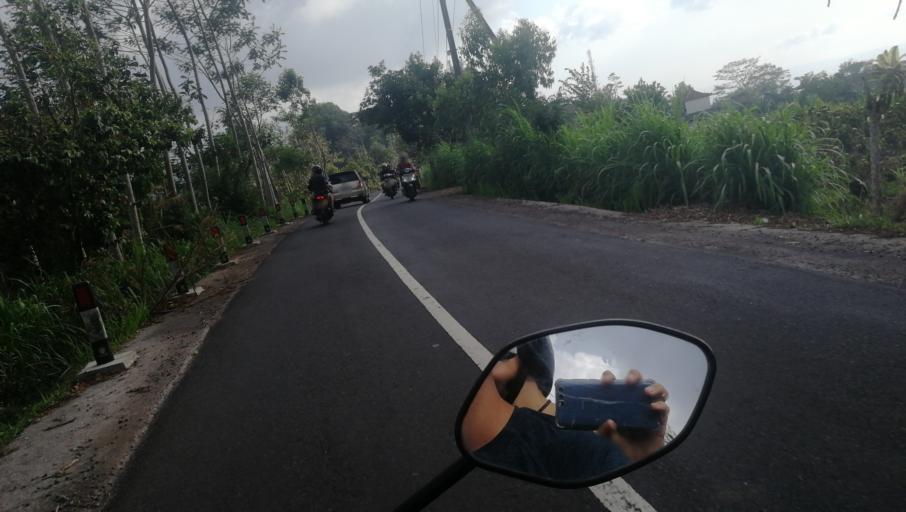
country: ID
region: Bali
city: Munduk
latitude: -8.2576
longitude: 115.0900
